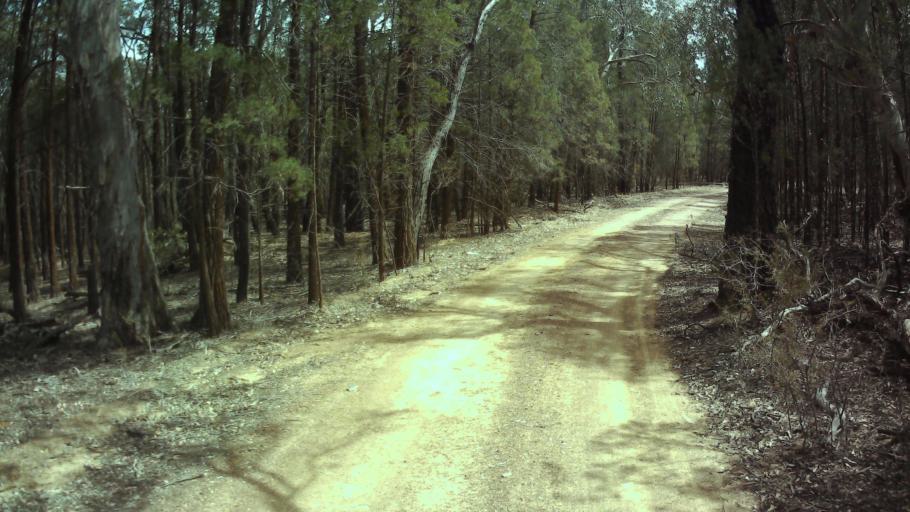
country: AU
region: New South Wales
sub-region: Weddin
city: Grenfell
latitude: -33.8880
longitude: 148.3829
